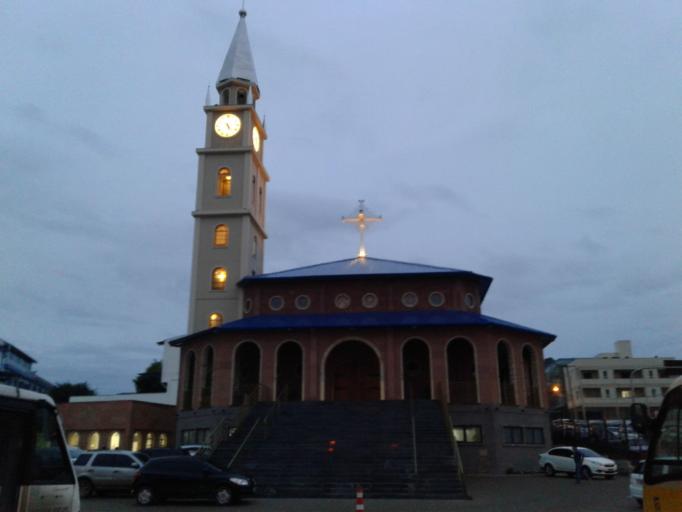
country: BR
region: Rio Grande do Sul
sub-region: Cachoeirinha
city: Cachoeirinha
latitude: -30.0131
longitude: -51.0980
